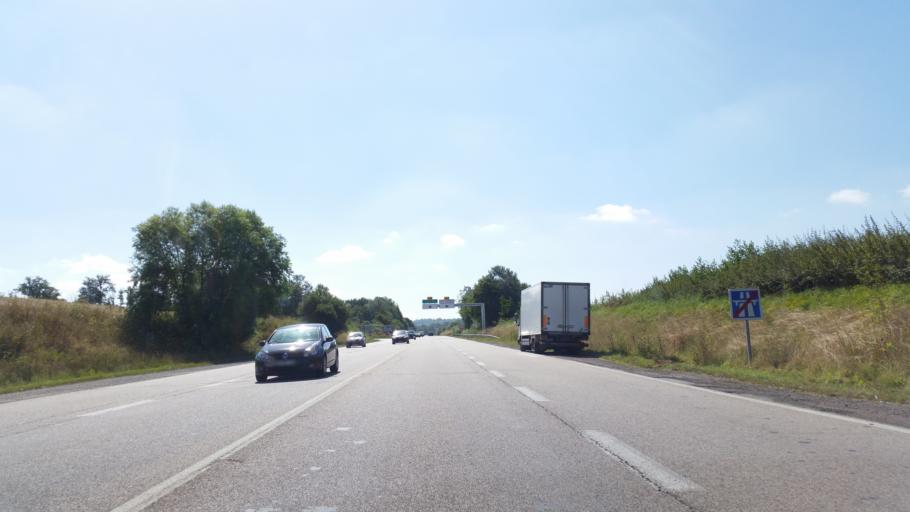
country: FR
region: Lower Normandy
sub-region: Departement du Calvados
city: Saint-Gatien-des-Bois
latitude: 49.2875
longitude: 0.2065
